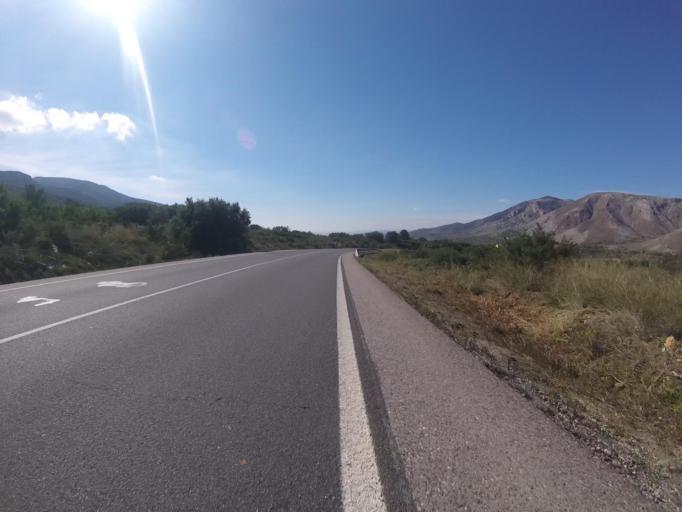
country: ES
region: Valencia
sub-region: Provincia de Castello
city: Sierra-Engarceran
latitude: 40.3136
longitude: -0.0330
